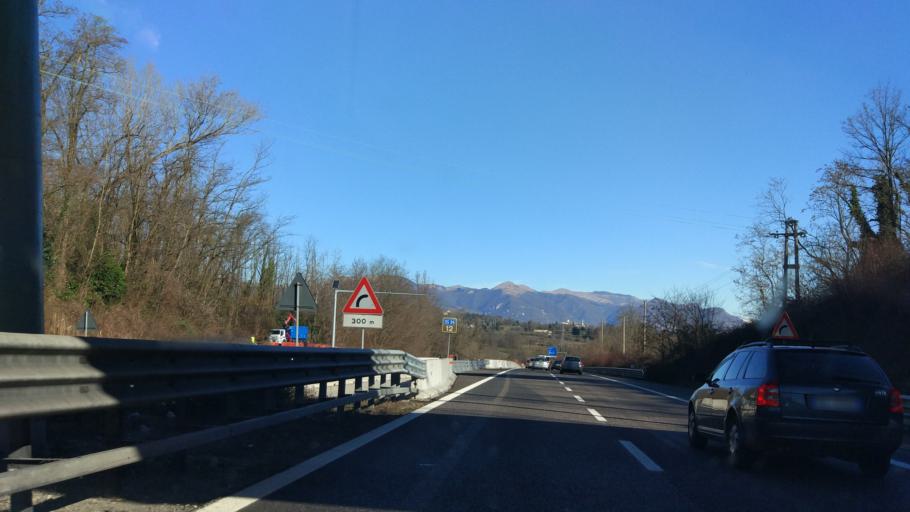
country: IT
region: Lombardy
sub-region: Provincia di Monza e Brianza
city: Briosco
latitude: 45.7094
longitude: 9.2280
